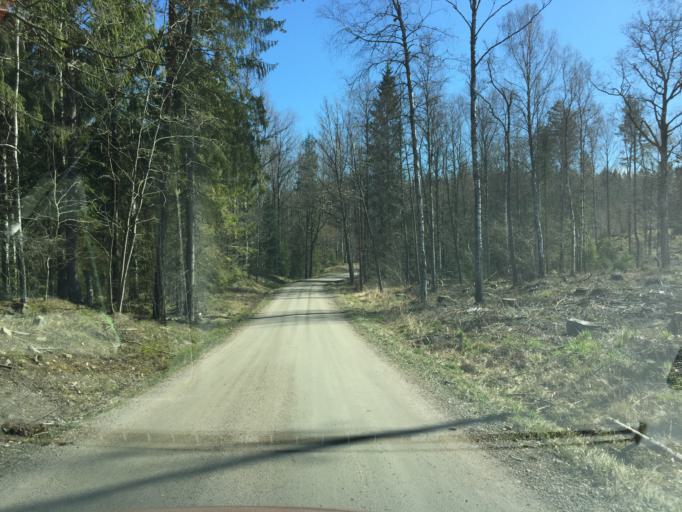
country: SE
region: OEstergoetland
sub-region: Finspangs Kommun
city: Finspang
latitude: 58.8910
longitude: 15.7305
